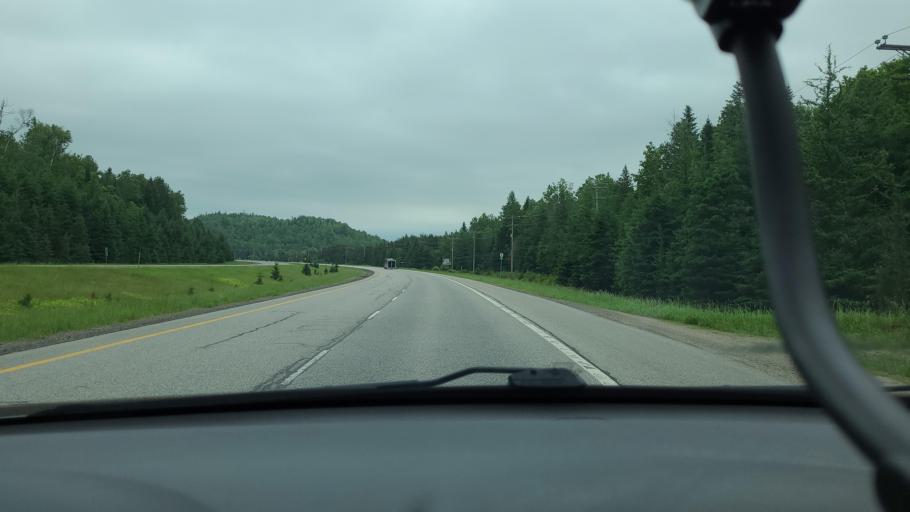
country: CA
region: Quebec
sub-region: Laurentides
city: Labelle
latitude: 46.2165
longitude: -74.7101
